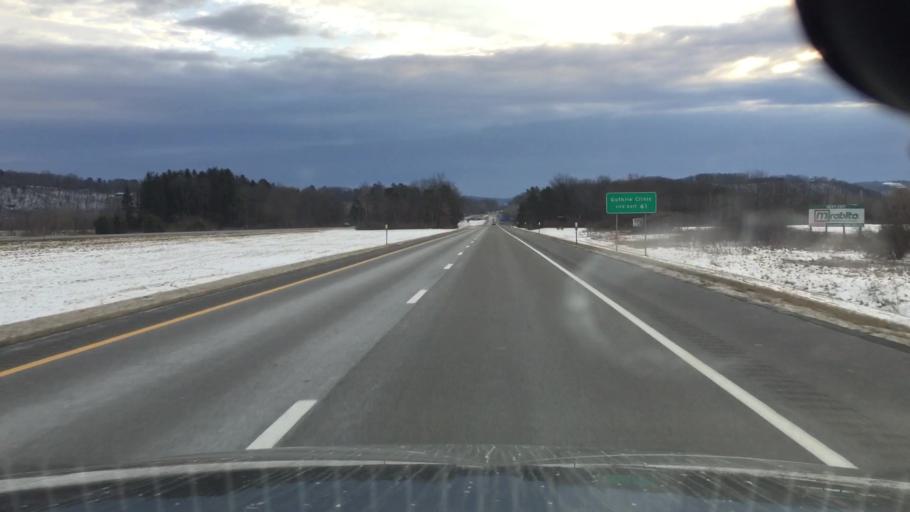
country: US
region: Pennsylvania
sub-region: Bradford County
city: South Waverly
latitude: 42.0007
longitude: -76.5735
